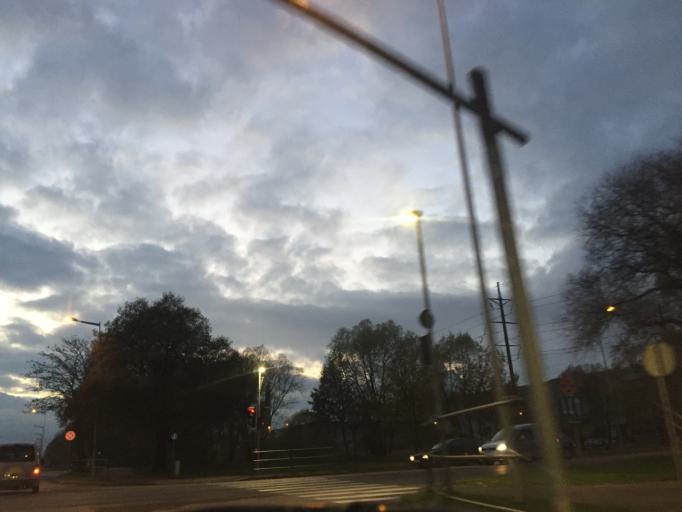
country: LV
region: Liepaja
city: Vec-Liepaja
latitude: 56.5352
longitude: 21.0562
